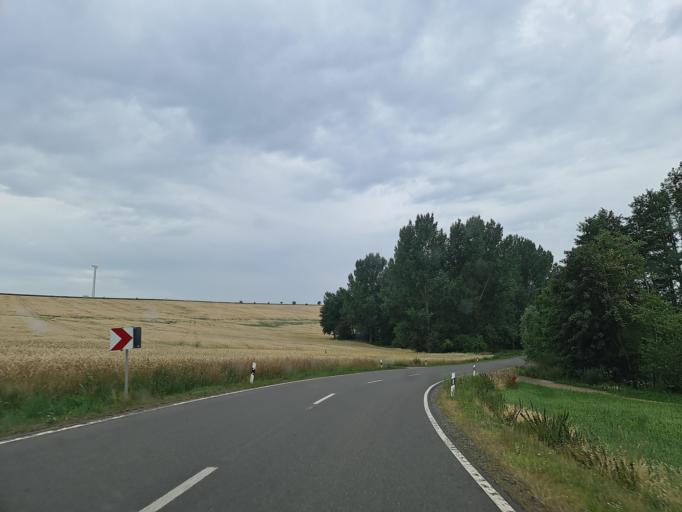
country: DE
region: Saxony
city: Leubsdorf
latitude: 50.7997
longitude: 13.1935
